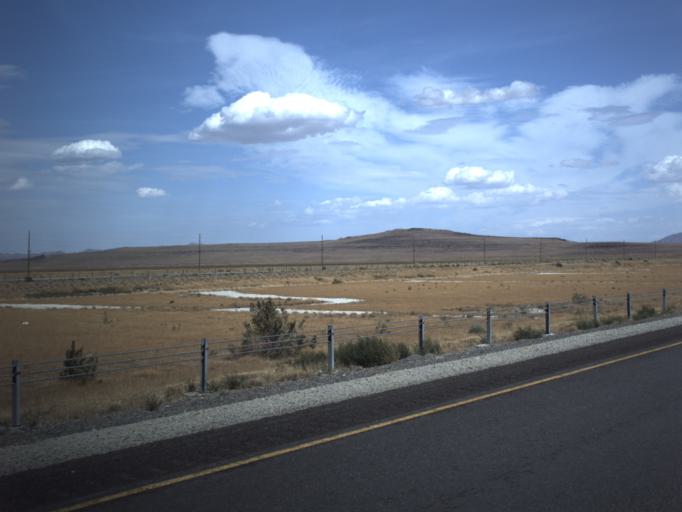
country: US
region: Utah
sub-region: Tooele County
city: Grantsville
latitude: 40.7257
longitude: -113.1948
